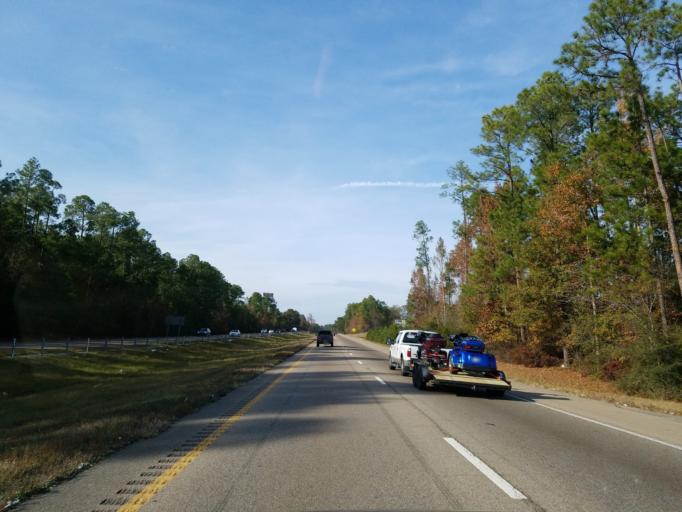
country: US
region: Mississippi
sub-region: Lamar County
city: West Hattiesburg
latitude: 31.2699
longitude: -89.3440
